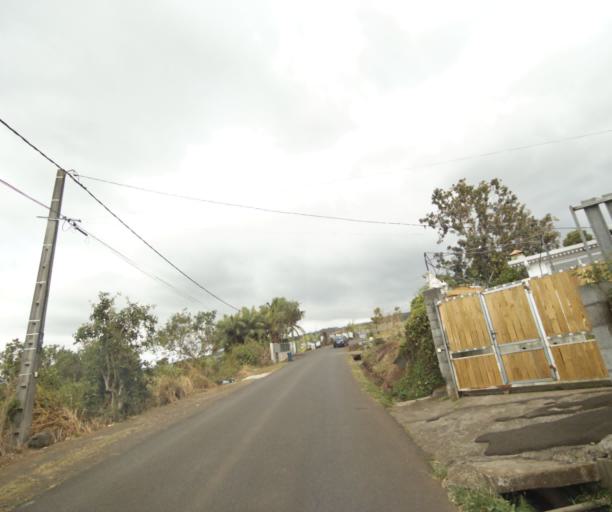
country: RE
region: Reunion
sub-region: Reunion
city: Saint-Paul
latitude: -21.0262
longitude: 55.3068
